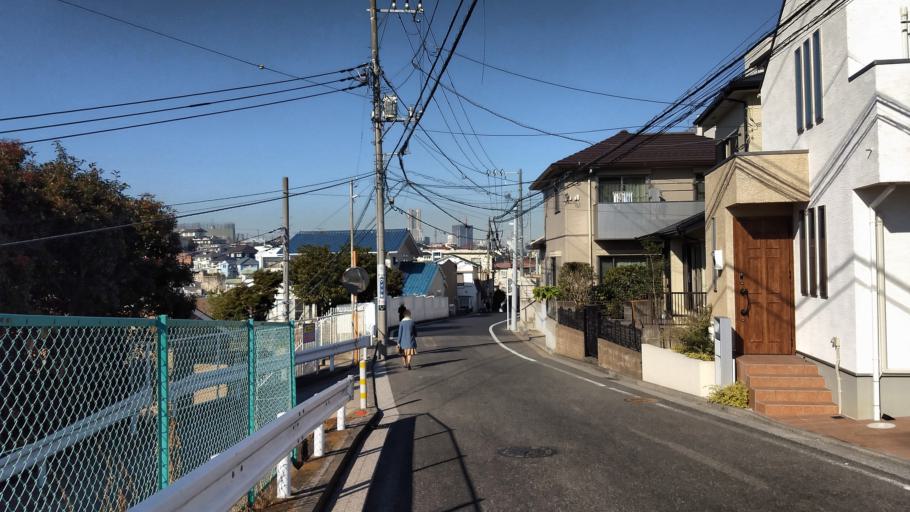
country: JP
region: Kanagawa
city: Yokohama
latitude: 35.4269
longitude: 139.6474
